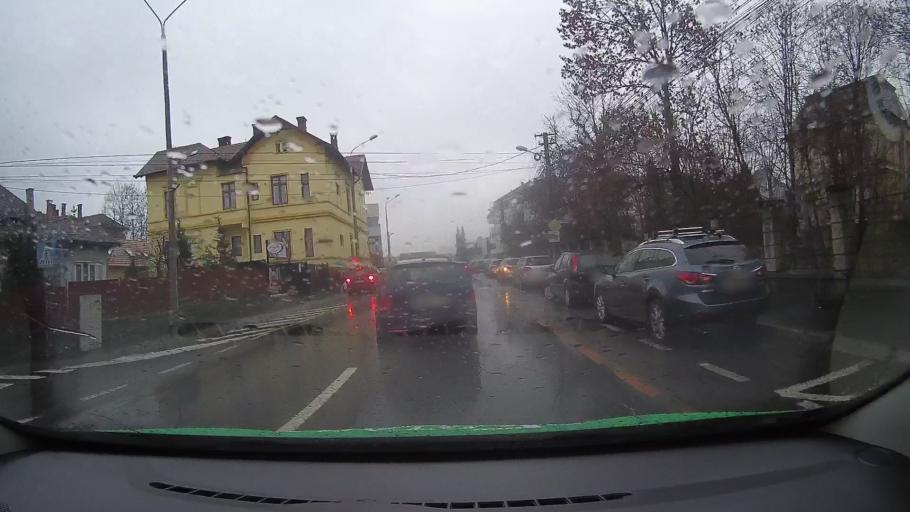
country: RO
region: Sibiu
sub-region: Municipiul Sibiu
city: Sibiu
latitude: 45.7888
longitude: 24.1417
